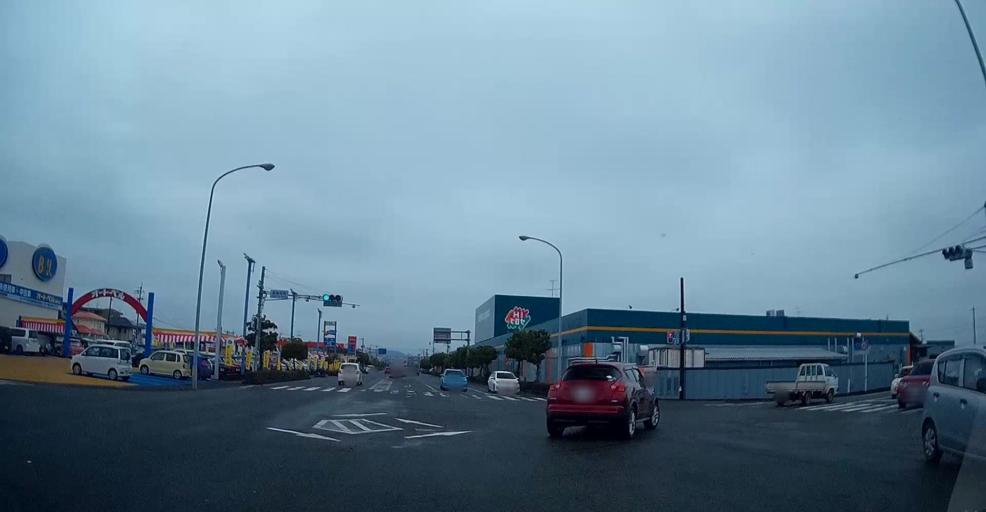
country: JP
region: Kumamoto
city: Kumamoto
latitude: 32.7491
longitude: 130.7396
